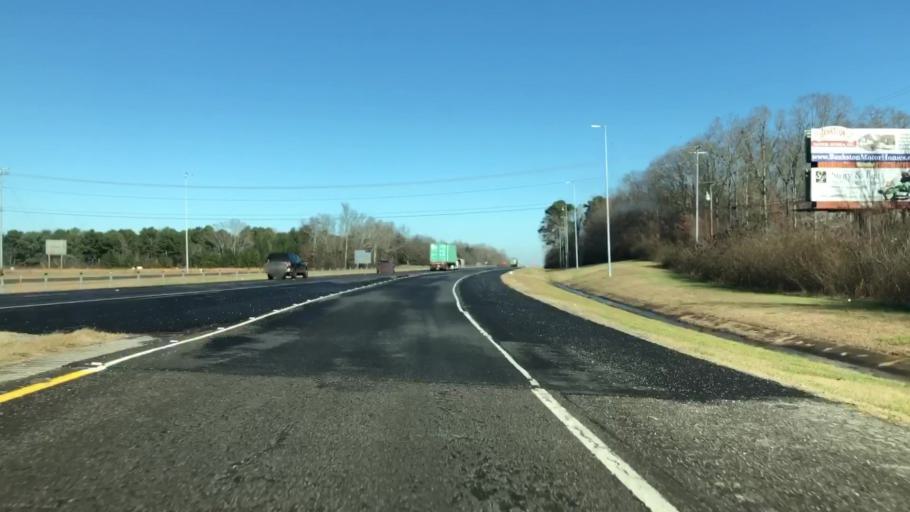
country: US
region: Alabama
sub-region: Limestone County
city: Athens
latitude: 34.7849
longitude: -86.9393
